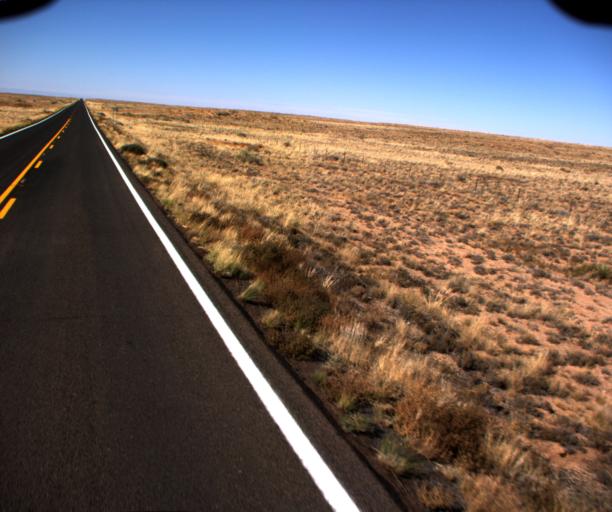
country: US
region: Arizona
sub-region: Coconino County
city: Tuba City
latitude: 35.9616
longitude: -110.9409
